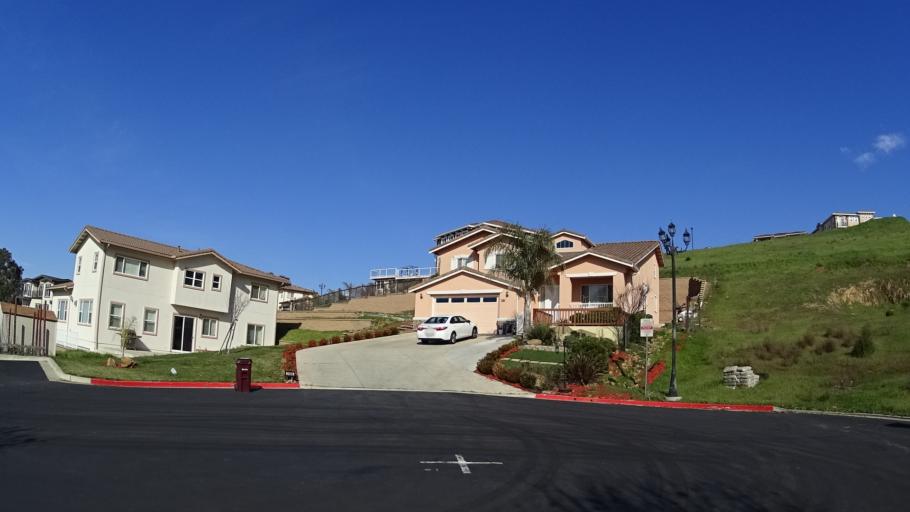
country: US
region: California
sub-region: Alameda County
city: Fairview
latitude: 37.6770
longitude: -122.0451
